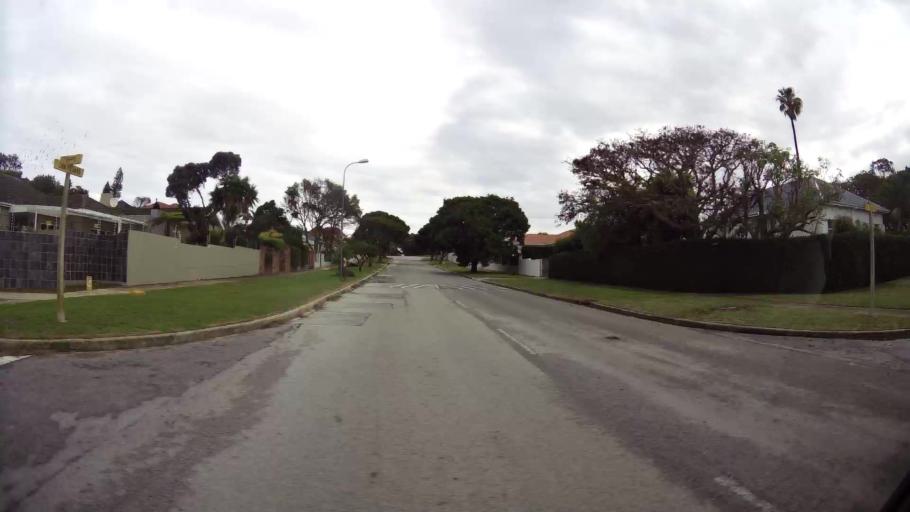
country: ZA
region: Eastern Cape
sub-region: Nelson Mandela Bay Metropolitan Municipality
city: Port Elizabeth
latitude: -33.9525
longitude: 25.5939
